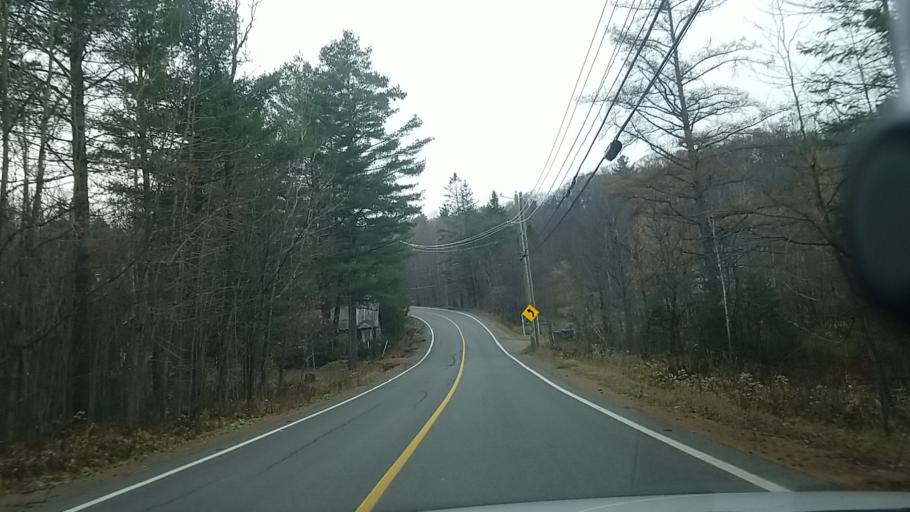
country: CA
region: Quebec
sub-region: Laurentides
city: Saint-Colomban
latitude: 45.7878
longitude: -74.1153
